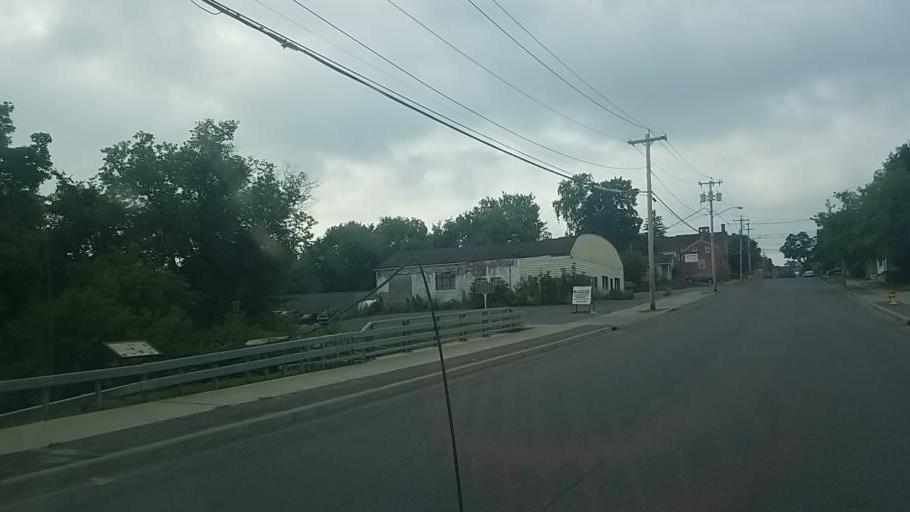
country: US
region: New York
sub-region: Fulton County
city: Johnstown
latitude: 43.0095
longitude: -74.3714
